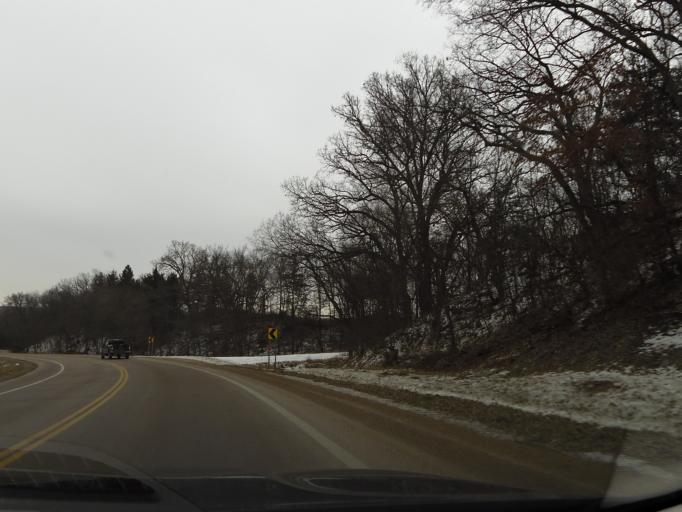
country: US
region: Minnesota
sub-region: Scott County
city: Jordan
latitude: 44.7064
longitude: -93.6497
